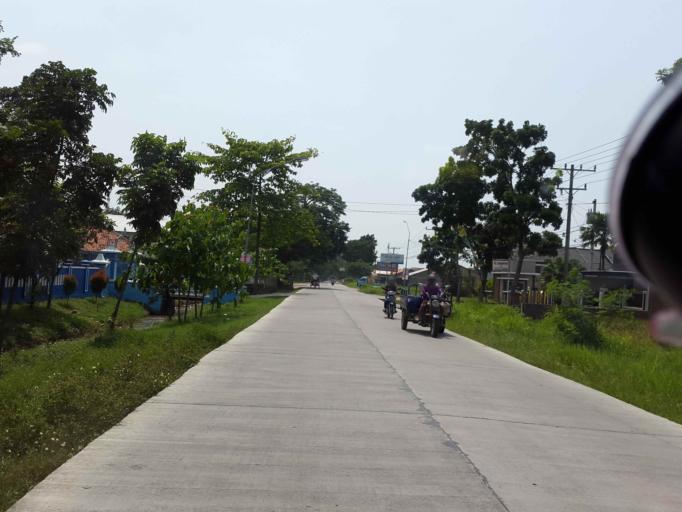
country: ID
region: Central Java
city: Pemalang
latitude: -6.9061
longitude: 109.3949
